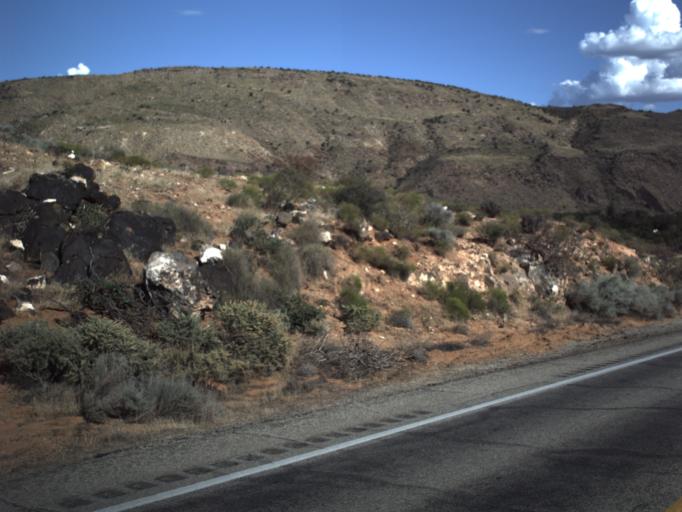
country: US
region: Utah
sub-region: Washington County
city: Toquerville
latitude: 37.2599
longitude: -113.2935
